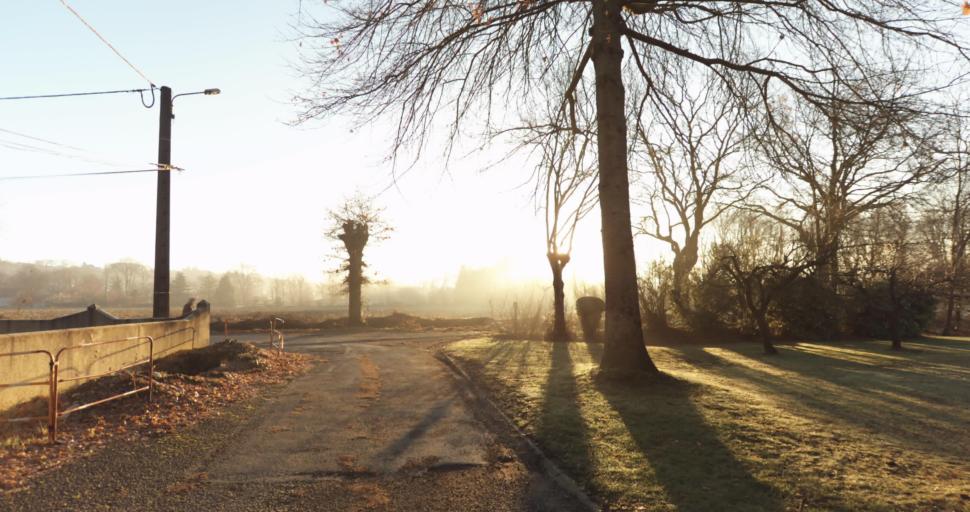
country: FR
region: Aquitaine
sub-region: Departement des Pyrenees-Atlantiques
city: Buros
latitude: 43.3269
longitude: -0.2875
